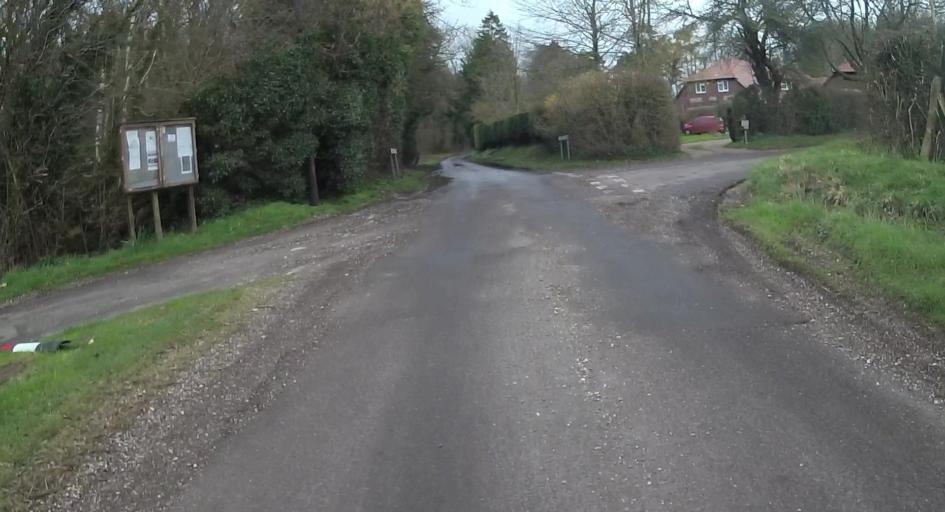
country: GB
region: England
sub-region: Hampshire
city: Kingsclere
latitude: 51.2744
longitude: -1.2018
